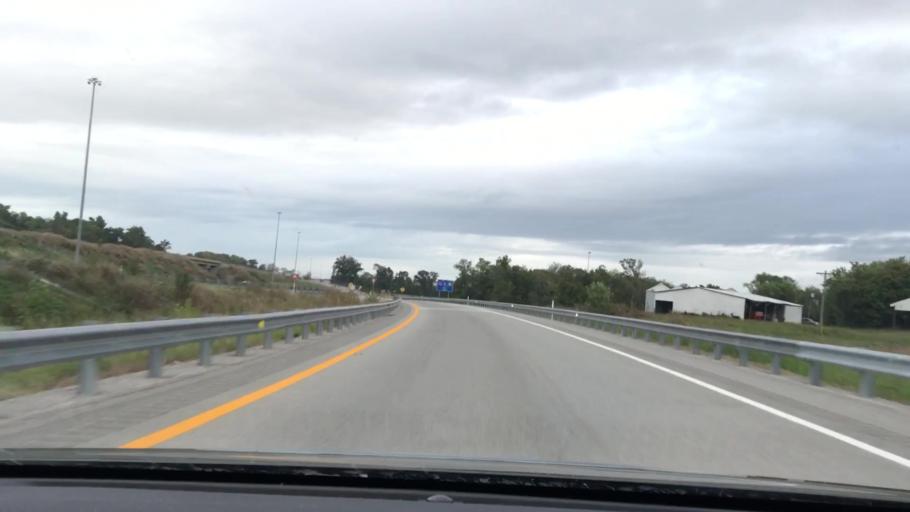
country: US
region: Kentucky
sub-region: Christian County
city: Hopkinsville
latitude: 36.8147
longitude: -87.4837
